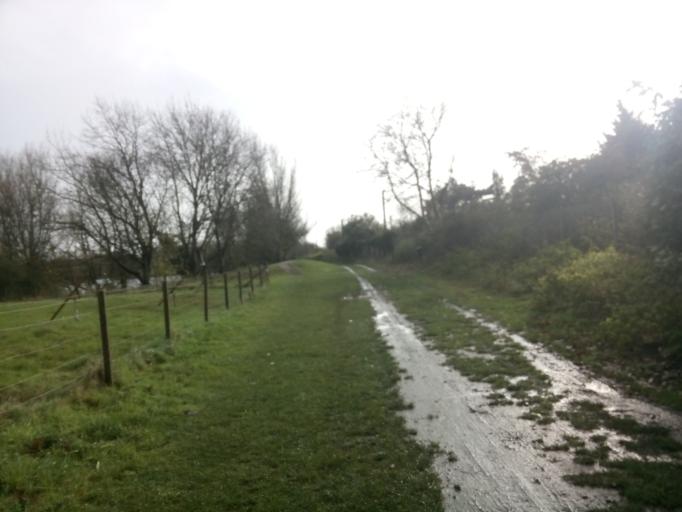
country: GB
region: England
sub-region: Suffolk
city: Needham Market
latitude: 52.1523
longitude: 1.0563
